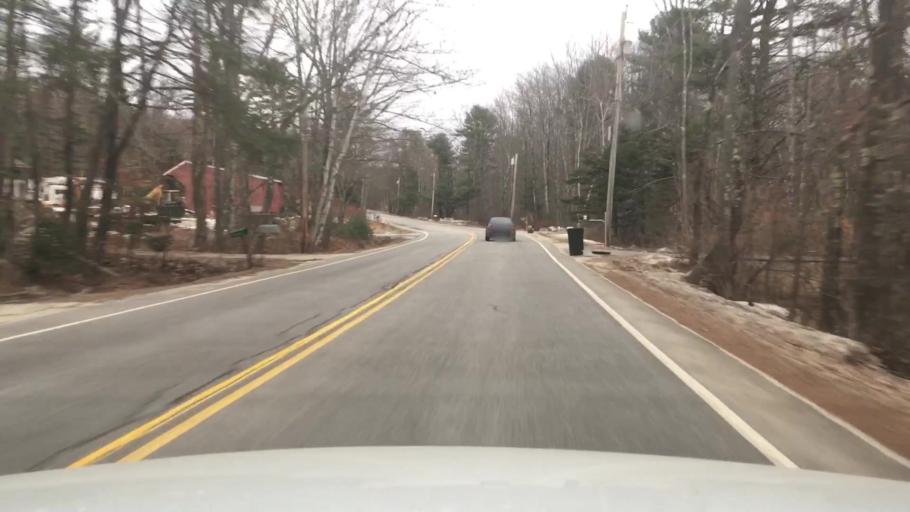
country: US
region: Maine
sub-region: Cumberland County
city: Freeport
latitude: 43.8792
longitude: -70.0423
